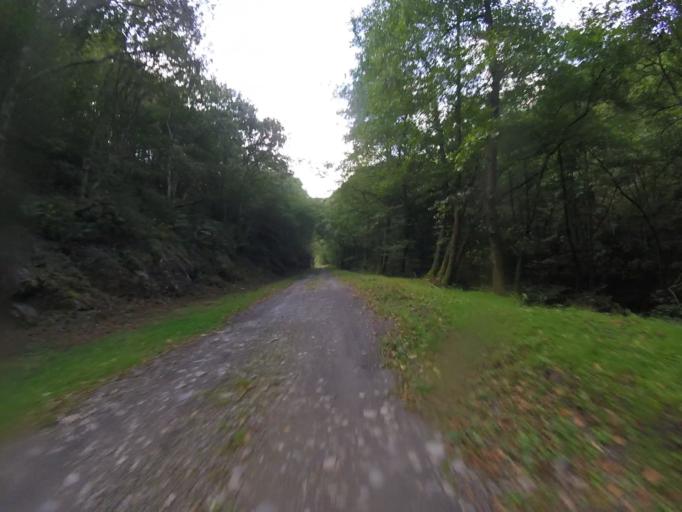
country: ES
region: Basque Country
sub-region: Provincia de Guipuzcoa
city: Berastegui
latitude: 43.1452
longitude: -1.9529
